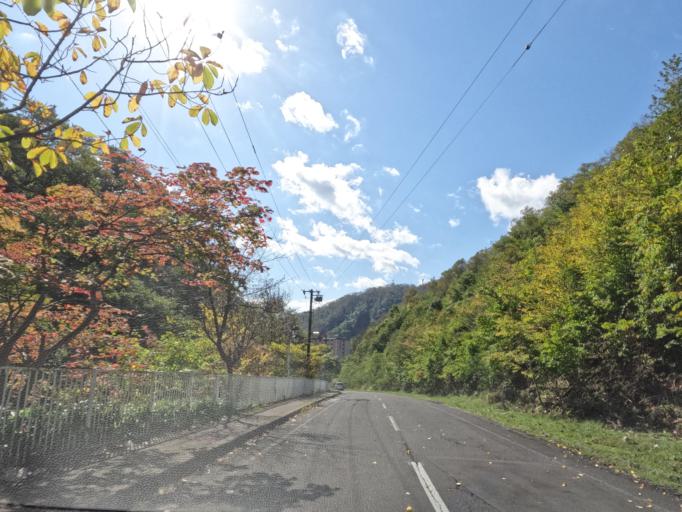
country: JP
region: Hokkaido
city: Shiraoi
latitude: 42.4993
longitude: 141.1414
